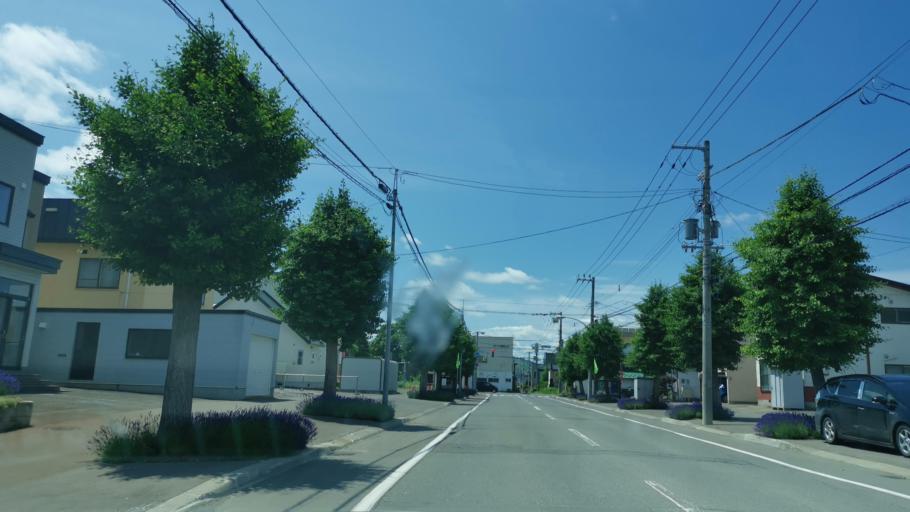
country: JP
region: Hokkaido
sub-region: Asahikawa-shi
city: Asahikawa
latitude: 43.7890
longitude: 142.3419
